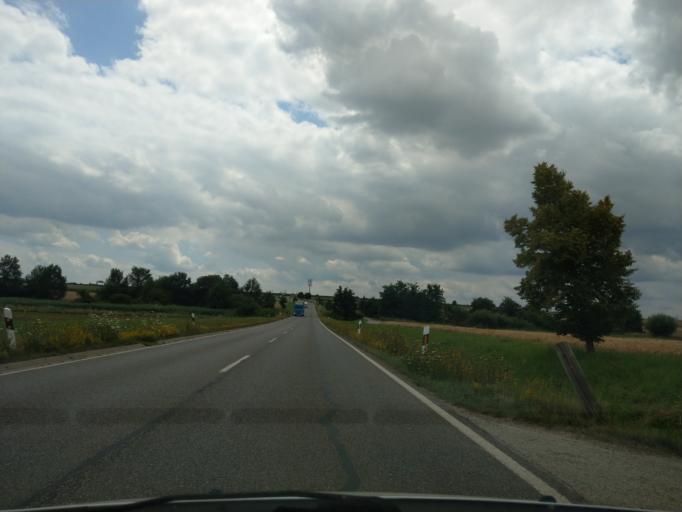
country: DE
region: Baden-Wuerttemberg
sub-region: Regierungsbezirk Stuttgart
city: Ostfildern
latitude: 48.7032
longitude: 9.2476
